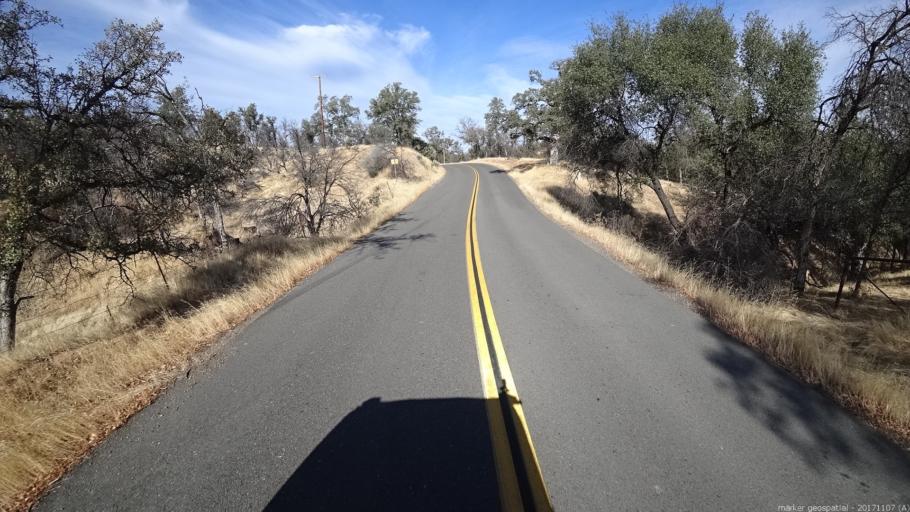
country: US
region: California
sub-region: Shasta County
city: Shasta
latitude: 40.4429
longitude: -122.5277
